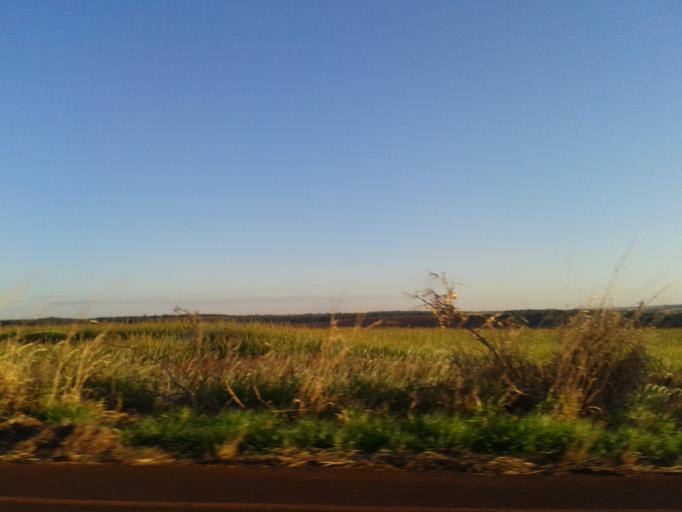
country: BR
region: Minas Gerais
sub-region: Centralina
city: Centralina
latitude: -18.7308
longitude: -49.2607
